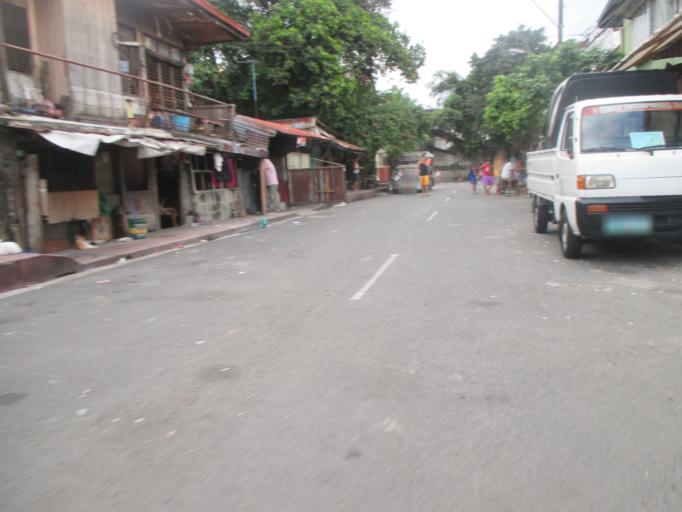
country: PH
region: Metro Manila
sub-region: Marikina
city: Calumpang
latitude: 14.6203
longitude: 121.0916
